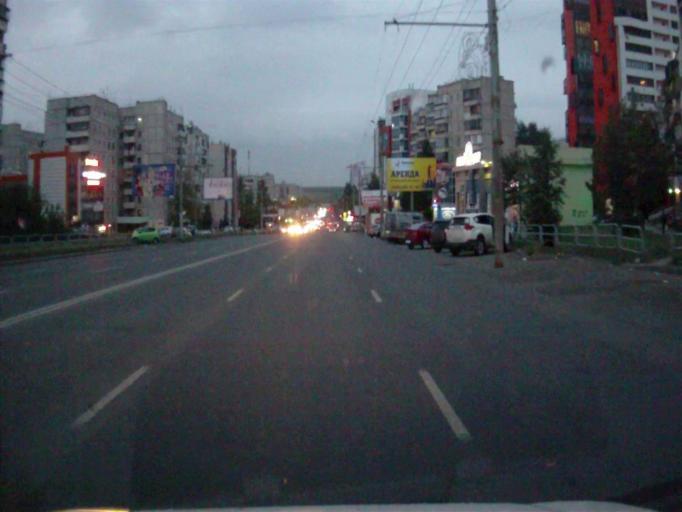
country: RU
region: Chelyabinsk
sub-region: Gorod Chelyabinsk
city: Chelyabinsk
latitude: 55.1861
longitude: 61.3325
